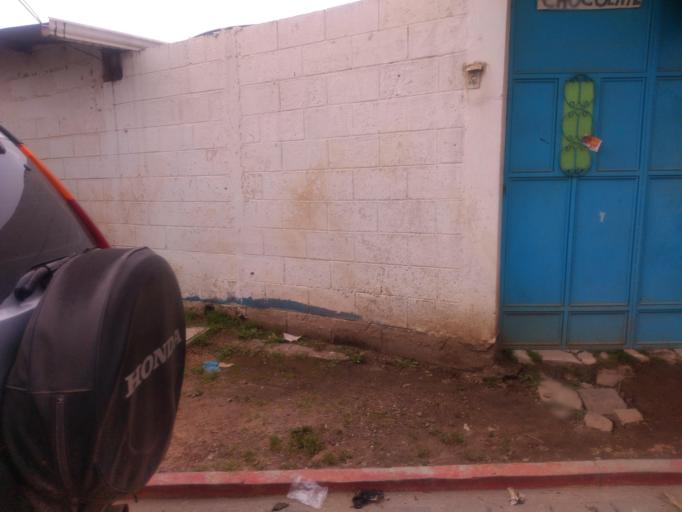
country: GT
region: Quetzaltenango
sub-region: Municipio de La Esperanza
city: La Esperanza
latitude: 14.8641
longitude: -91.5714
